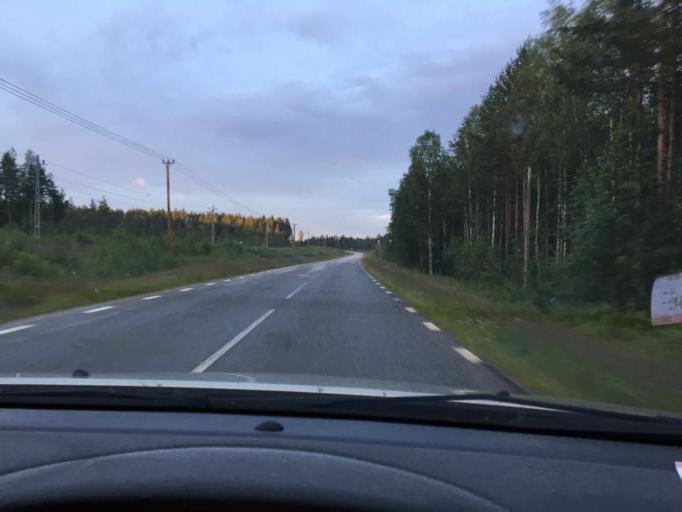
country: SE
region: Norrbotten
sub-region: Kalix Kommun
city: Toere
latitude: 66.0536
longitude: 22.5684
